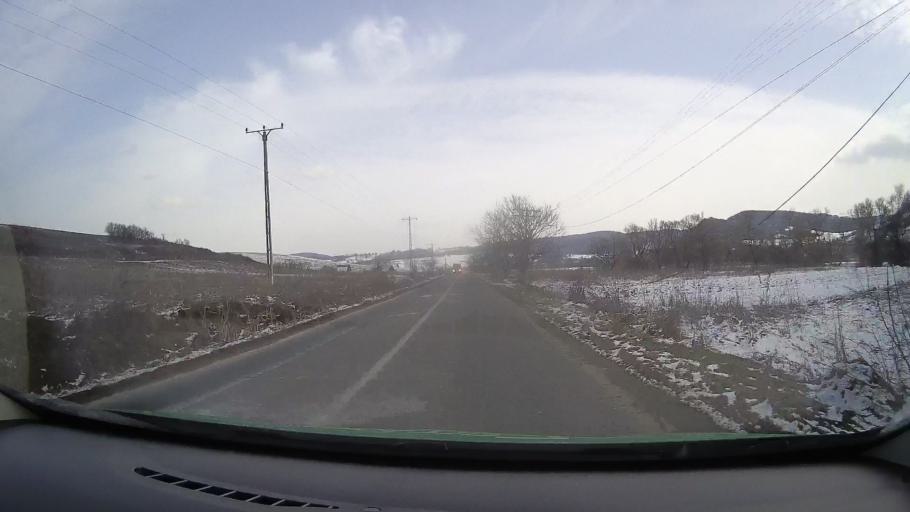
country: RO
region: Mures
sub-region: Comuna Apold
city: Saes
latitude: 46.1451
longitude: 24.7784
